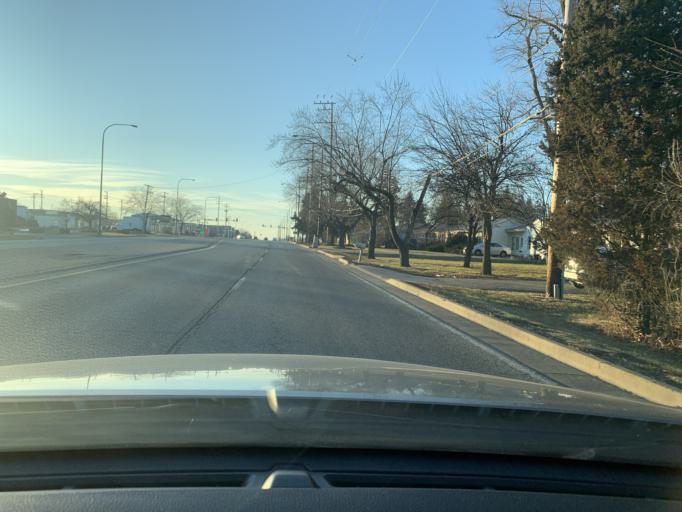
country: US
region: Illinois
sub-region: Cook County
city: Elk Grove Village
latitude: 41.9930
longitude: -87.9769
